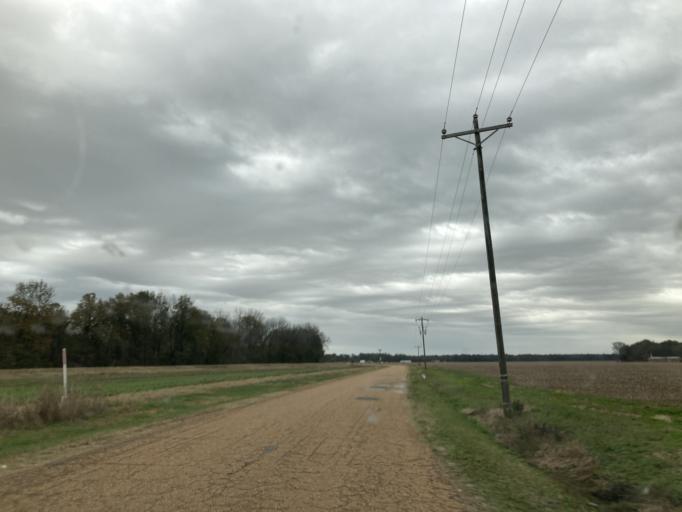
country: US
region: Mississippi
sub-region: Yazoo County
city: Yazoo City
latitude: 32.9811
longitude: -90.4205
